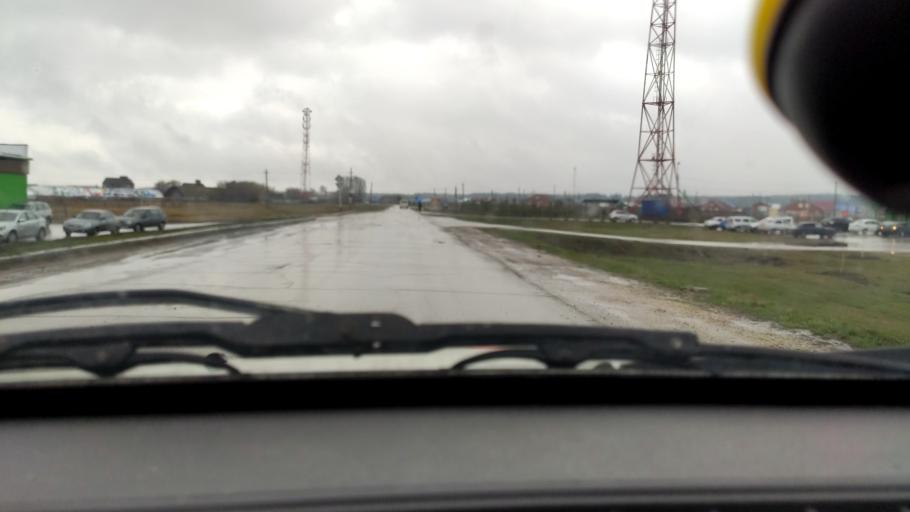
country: RU
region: Samara
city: Povolzhskiy
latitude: 53.6474
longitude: 49.6785
